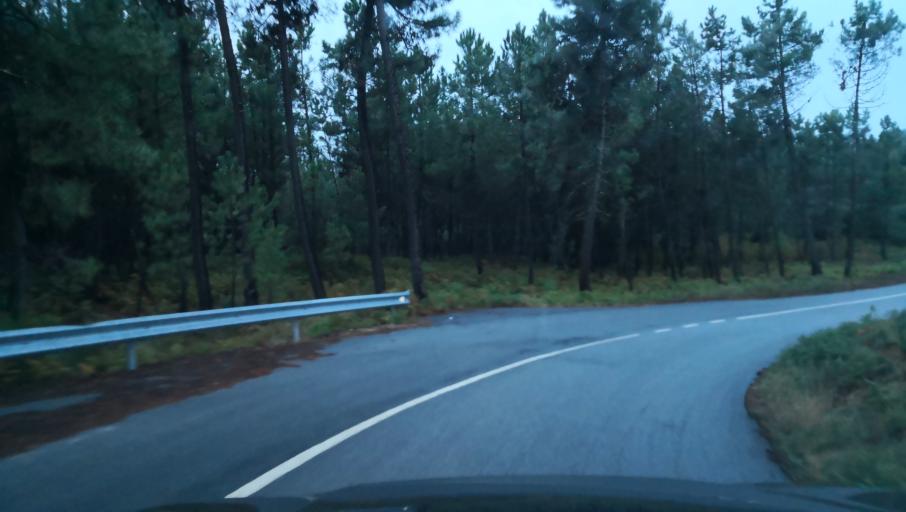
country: PT
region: Vila Real
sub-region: Sabrosa
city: Sabrosa
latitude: 41.2759
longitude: -7.5950
